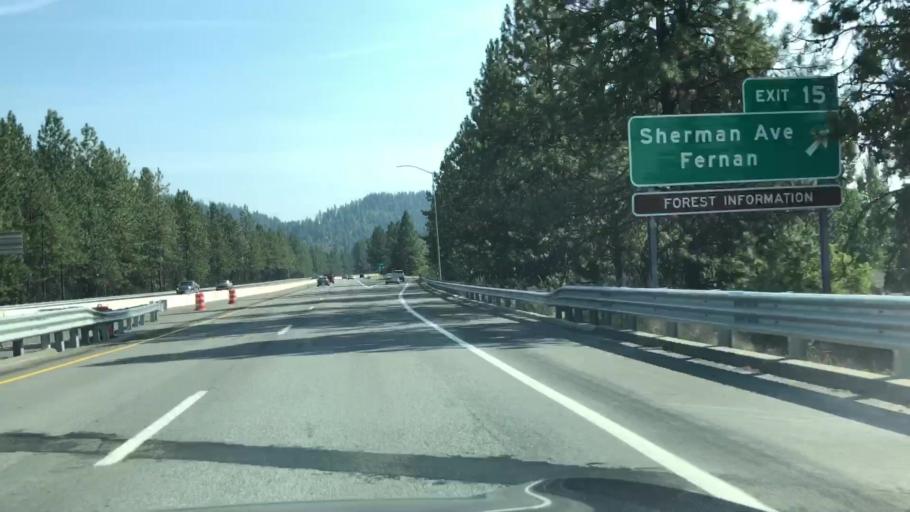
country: US
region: Idaho
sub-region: Kootenai County
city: Coeur d'Alene
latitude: 47.6790
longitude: -116.7555
